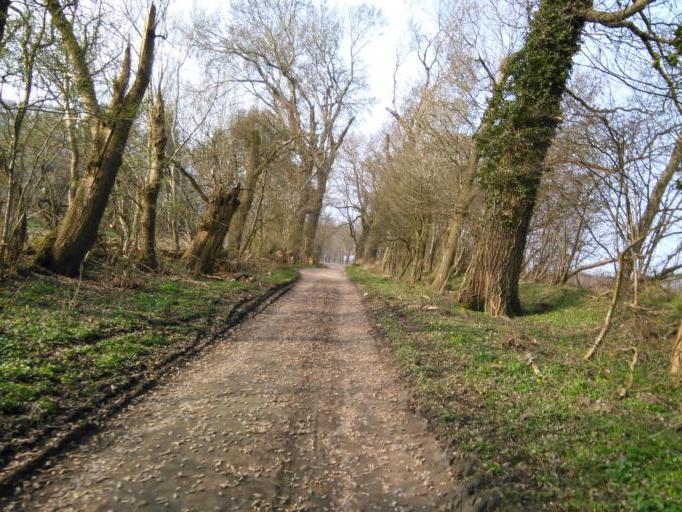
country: DK
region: Central Jutland
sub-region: Arhus Kommune
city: Beder
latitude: 56.0847
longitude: 10.2211
